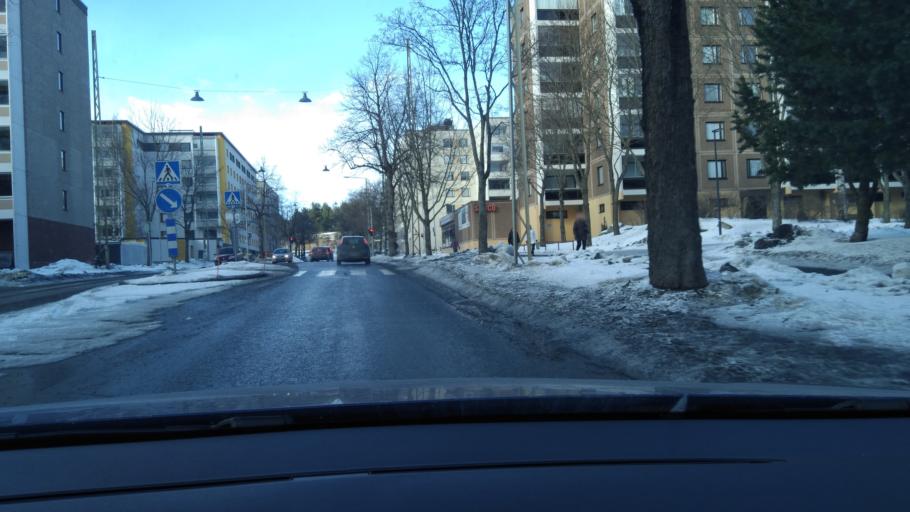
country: FI
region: Pirkanmaa
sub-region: Tampere
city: Tampere
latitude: 61.5046
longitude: 23.7796
